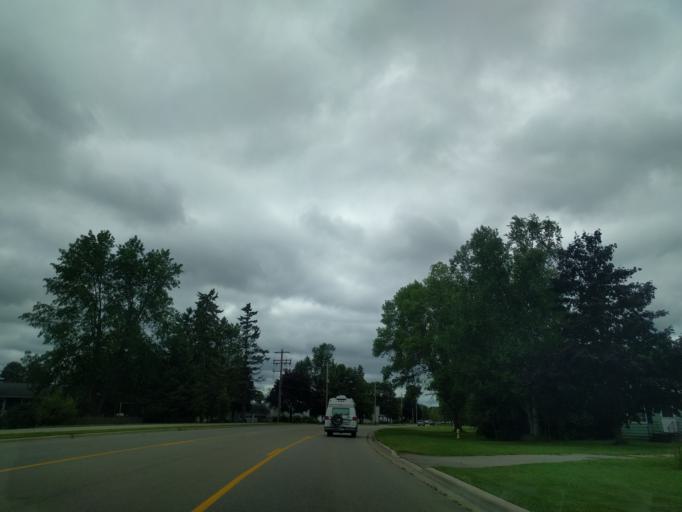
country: US
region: Michigan
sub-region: Menominee County
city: Menominee
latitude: 45.1401
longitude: -87.6039
